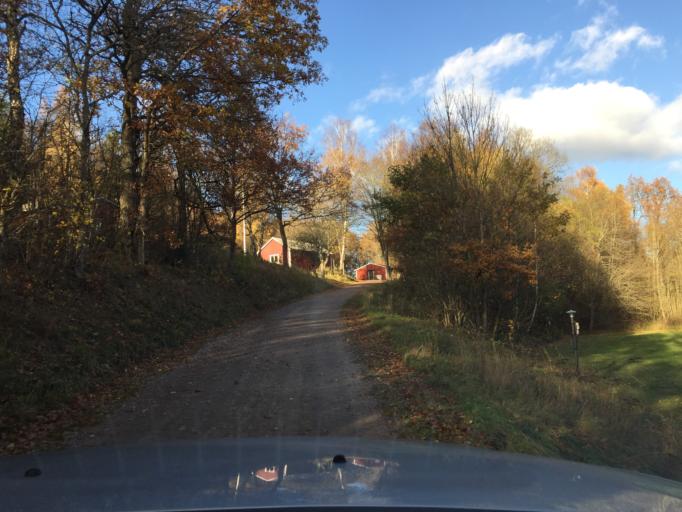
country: SE
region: Skane
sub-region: Hassleholms Kommun
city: Tormestorp
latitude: 56.0762
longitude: 13.7355
